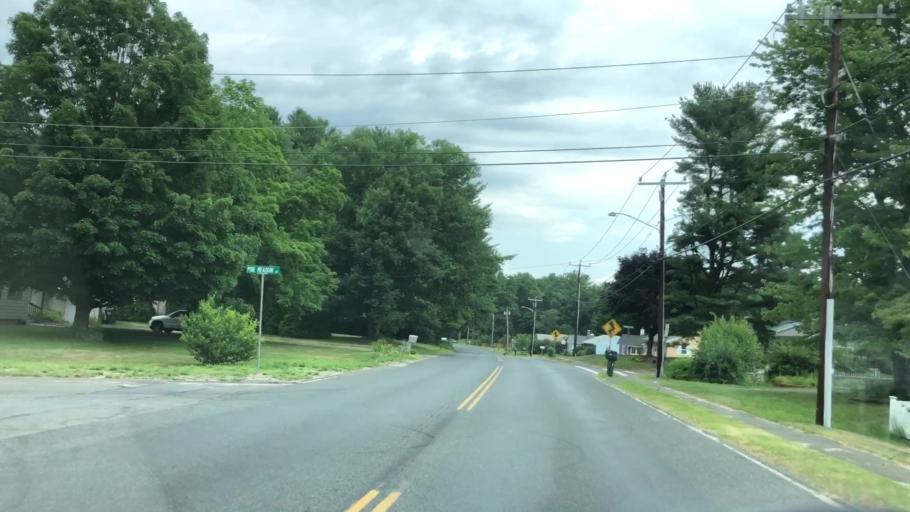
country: US
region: Massachusetts
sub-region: Hampshire County
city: Easthampton
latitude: 42.2330
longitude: -72.6858
